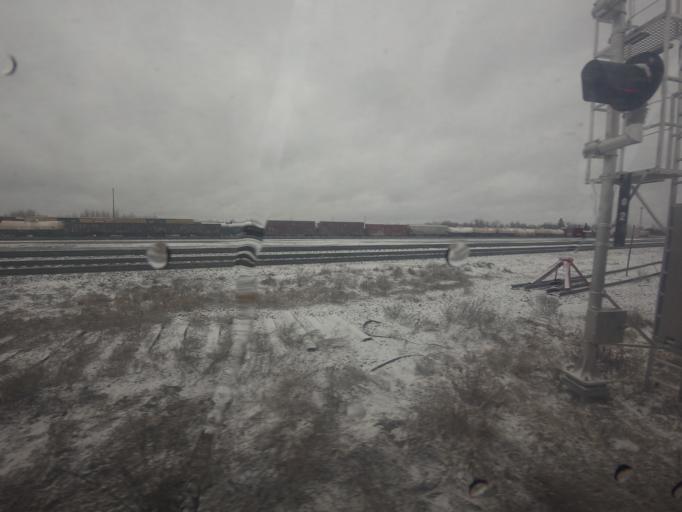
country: CA
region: Ontario
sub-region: Lanark County
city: Smiths Falls
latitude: 44.9047
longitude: -76.0150
